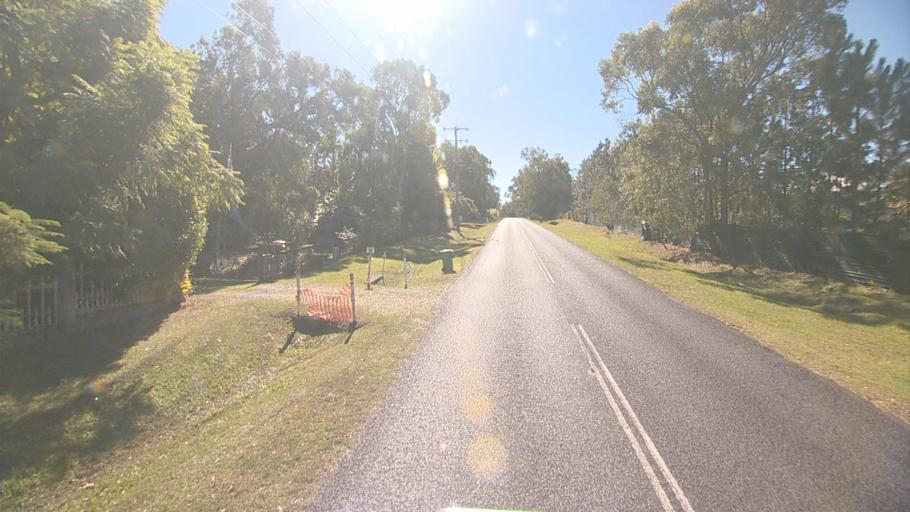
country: AU
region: Queensland
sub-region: Logan
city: Park Ridge South
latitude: -27.7147
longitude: 153.0580
